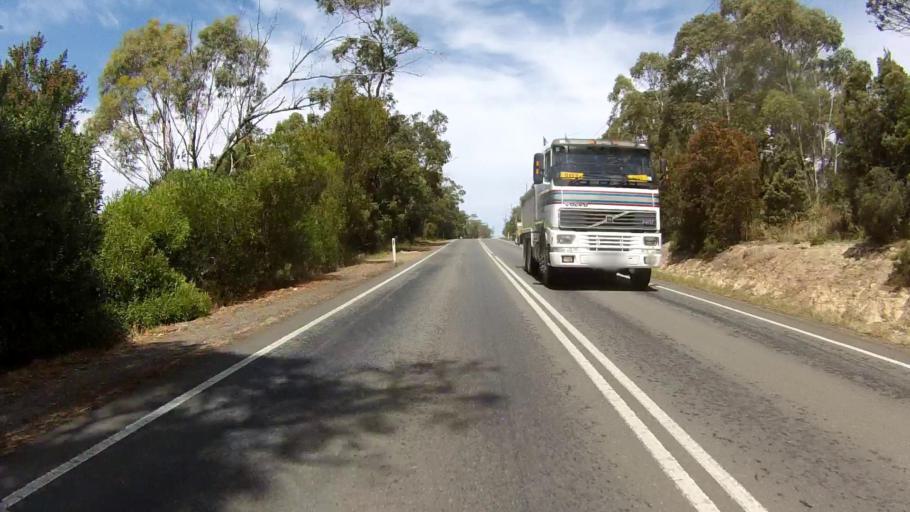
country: AU
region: Tasmania
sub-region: Clarence
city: Sandford
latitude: -42.9667
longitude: 147.5029
